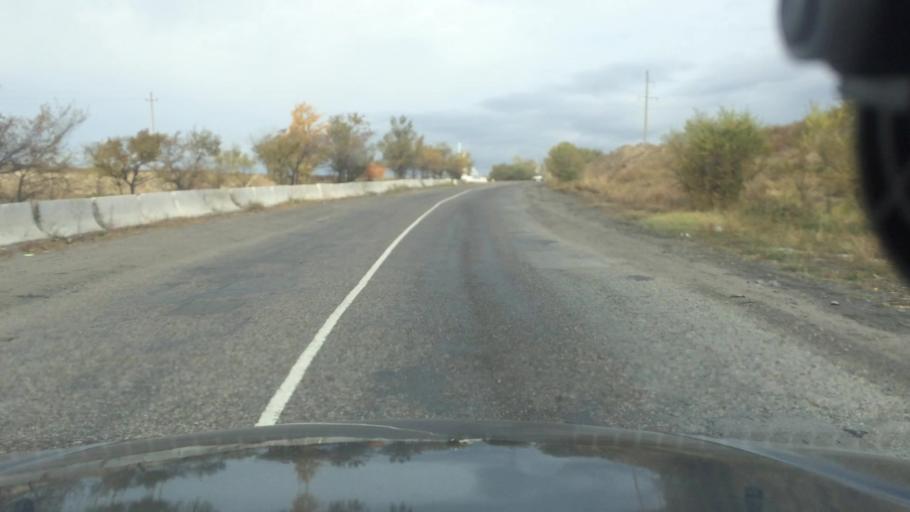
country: KG
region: Ysyk-Koel
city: Karakol
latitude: 42.5973
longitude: 78.3765
